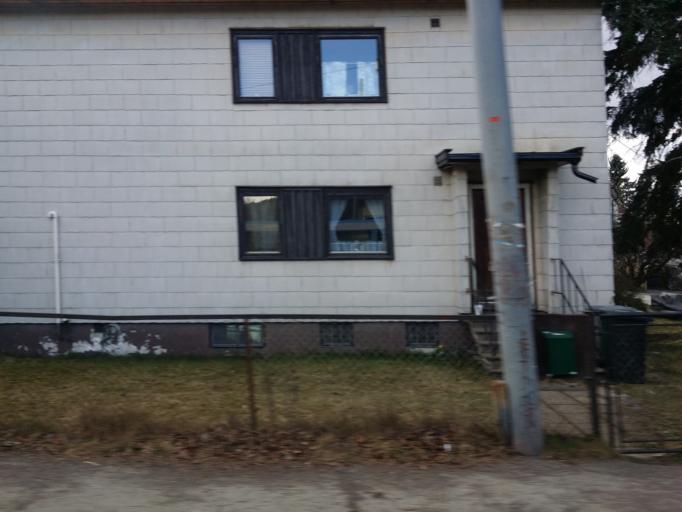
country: NO
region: Oslo
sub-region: Oslo
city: Oslo
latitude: 59.9533
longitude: 10.7855
